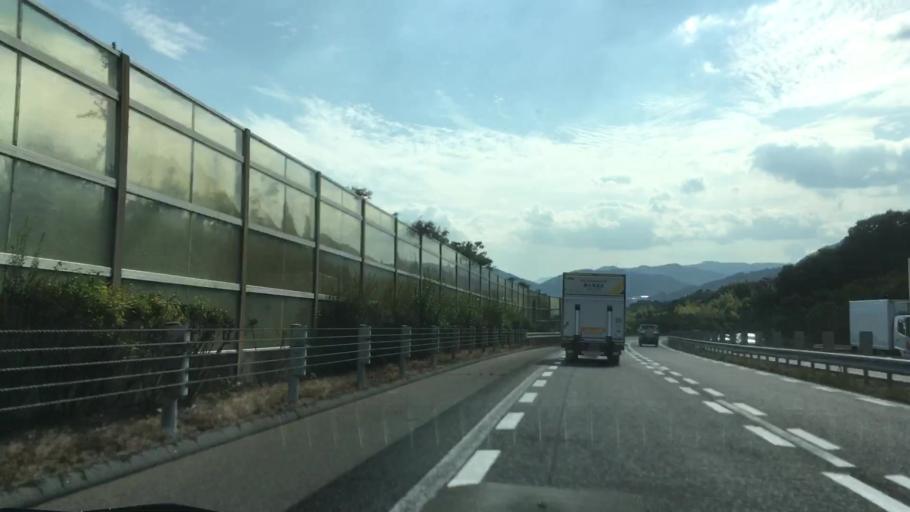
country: JP
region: Hiroshima
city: Ono-hara
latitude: 34.2675
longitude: 132.2422
